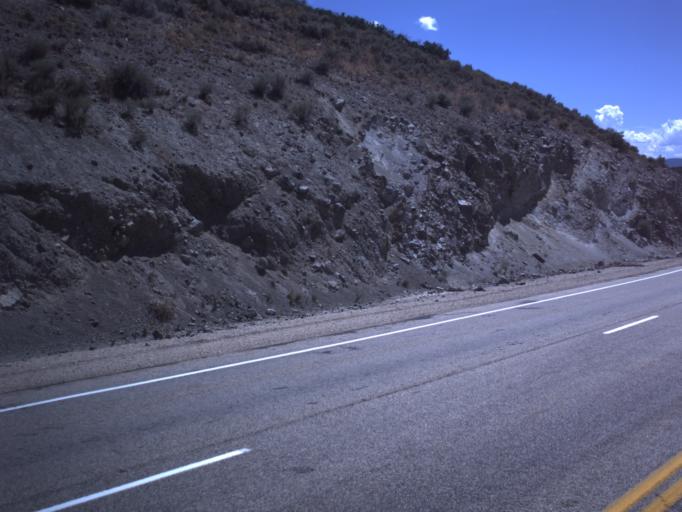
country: US
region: Utah
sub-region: Wasatch County
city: Heber
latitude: 40.5892
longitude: -111.4221
